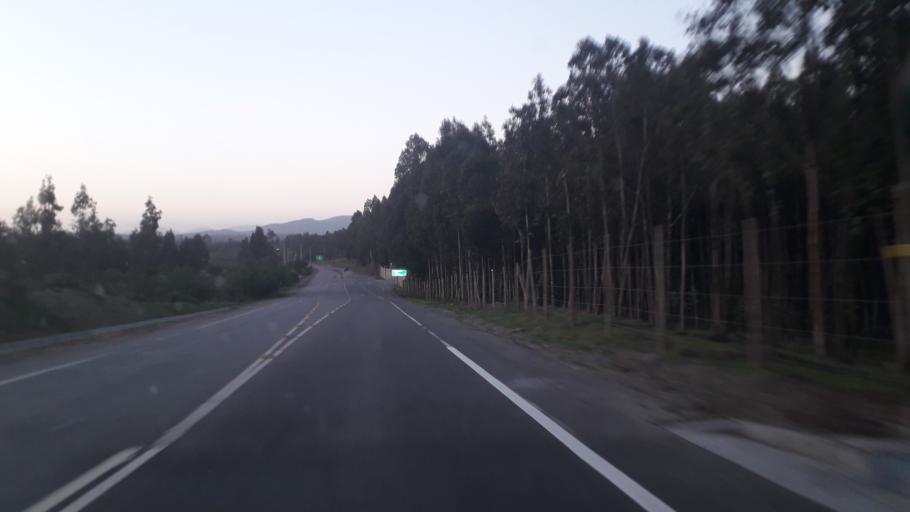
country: CL
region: Valparaiso
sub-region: Provincia de Quillota
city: Hacienda La Calera
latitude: -32.7479
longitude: -71.4185
